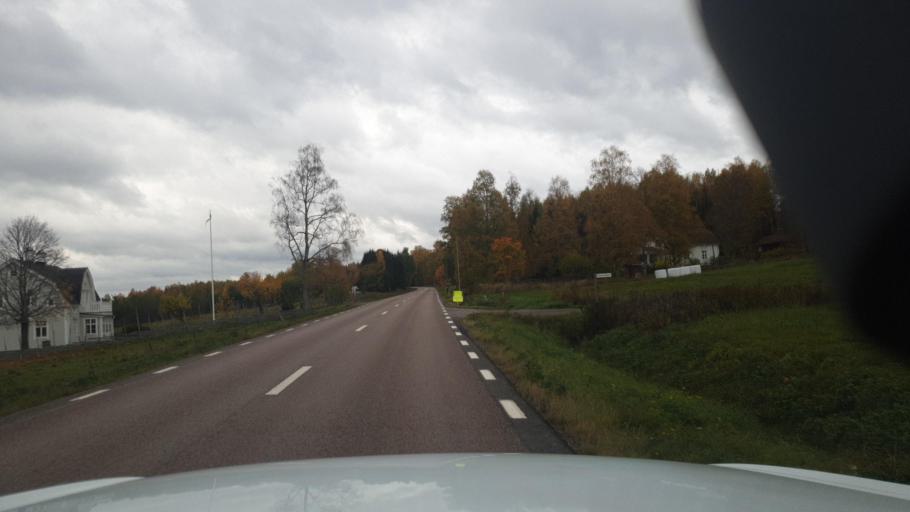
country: SE
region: Vaermland
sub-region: Sunne Kommun
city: Sunne
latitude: 59.8935
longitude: 12.9193
